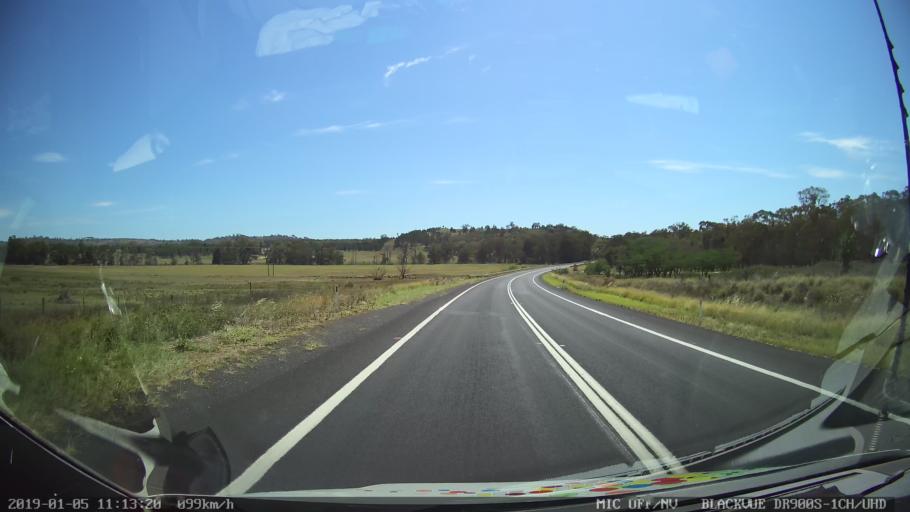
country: AU
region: New South Wales
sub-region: Warrumbungle Shire
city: Coonabarabran
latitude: -31.3714
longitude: 149.2693
